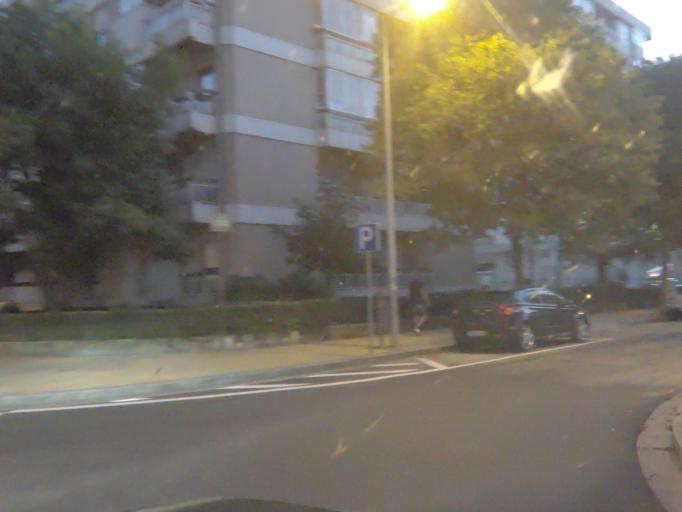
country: PT
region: Porto
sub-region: Matosinhos
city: Senhora da Hora
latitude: 41.1623
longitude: -8.6436
